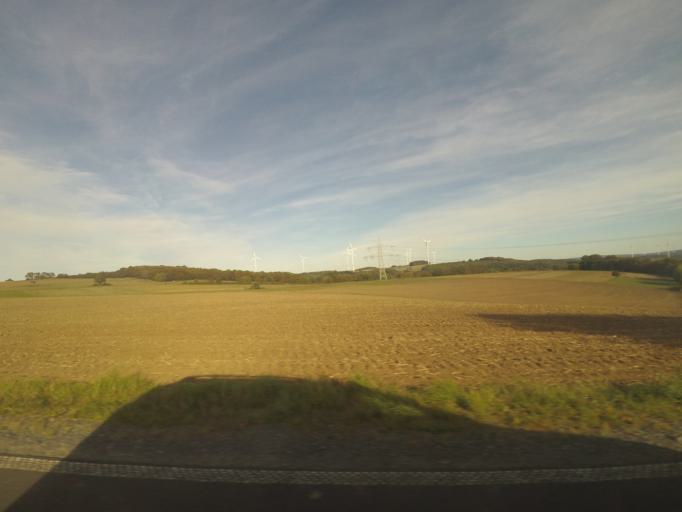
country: DE
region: Hesse
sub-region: Regierungsbezirk Giessen
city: Freiensteinau
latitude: 50.3928
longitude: 9.4431
